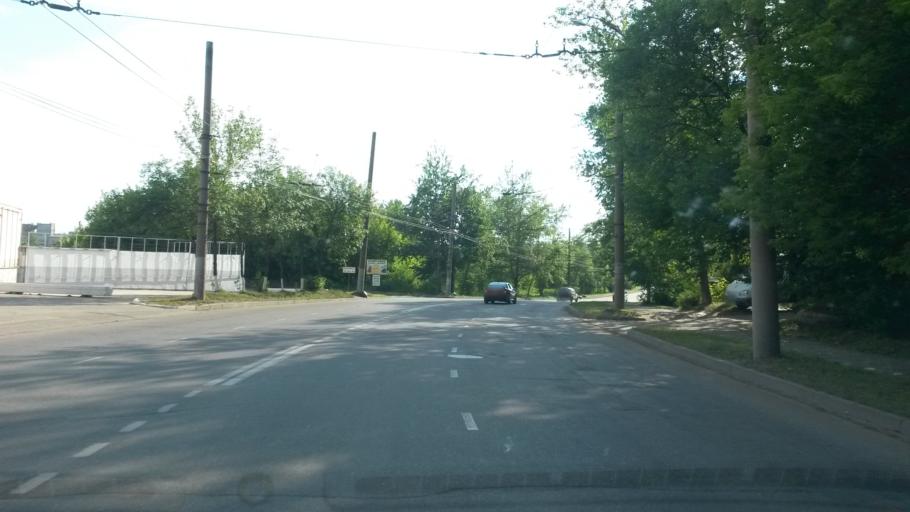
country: RU
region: Ivanovo
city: Kokhma
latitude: 56.9673
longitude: 41.0477
